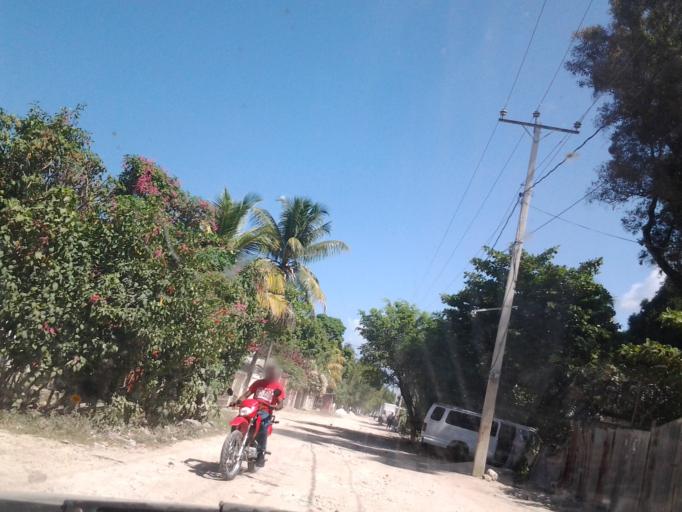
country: HT
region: Ouest
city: Grangwav
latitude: 18.4265
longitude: -72.7742
